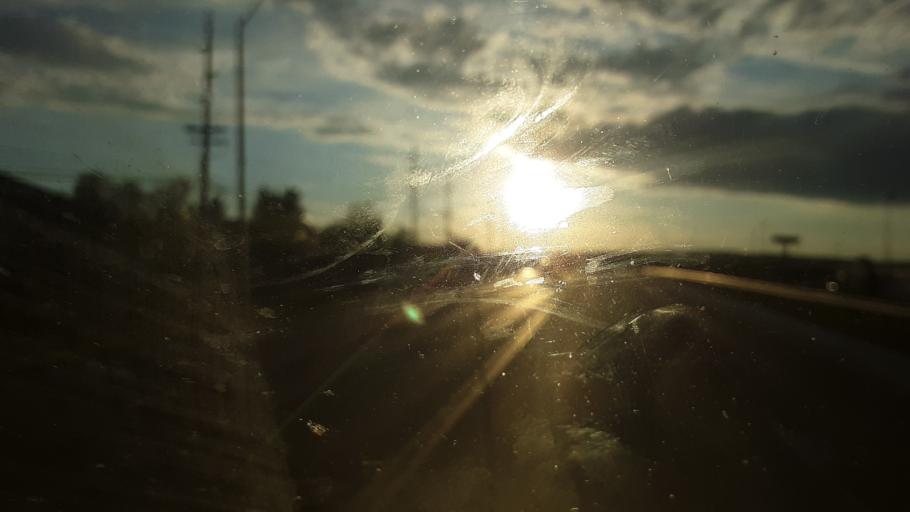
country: US
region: Maine
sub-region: Aroostook County
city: Presque Isle
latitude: 46.6984
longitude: -68.0056
